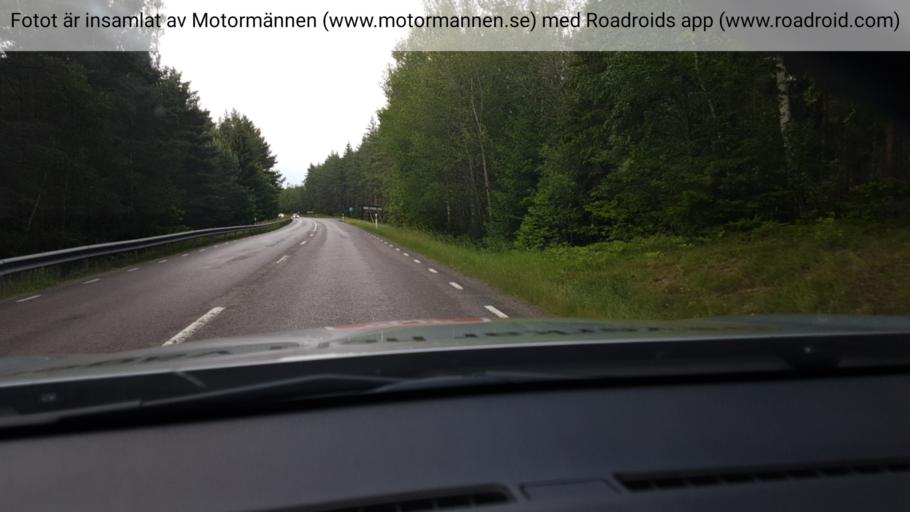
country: SE
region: Vaestra Goetaland
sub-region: Hjo Kommun
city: Hjo
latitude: 58.1955
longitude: 14.2064
